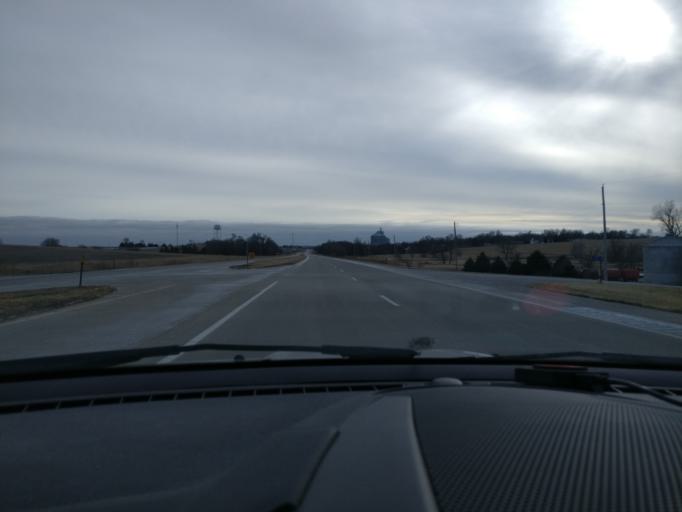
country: US
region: Nebraska
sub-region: Saunders County
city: Wahoo
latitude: 41.0698
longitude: -96.6404
